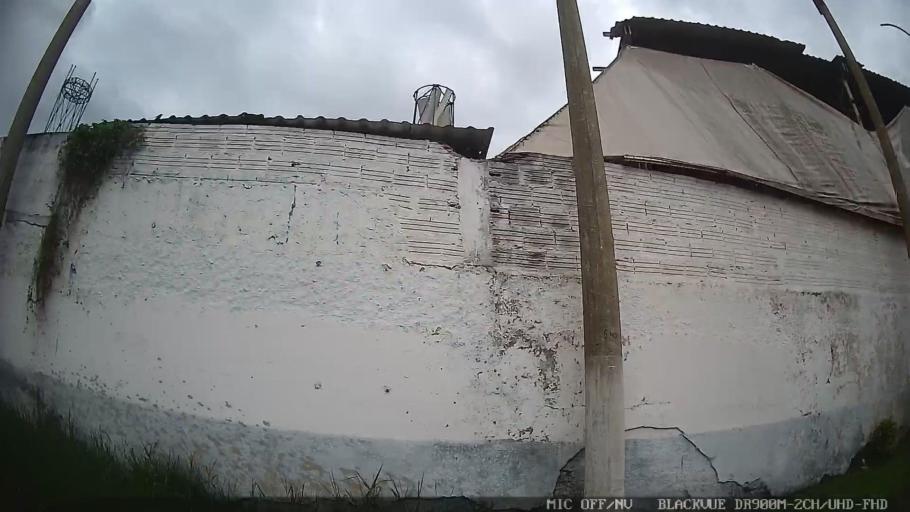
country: BR
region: Sao Paulo
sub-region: Guaruja
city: Guaruja
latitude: -23.9966
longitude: -46.2920
